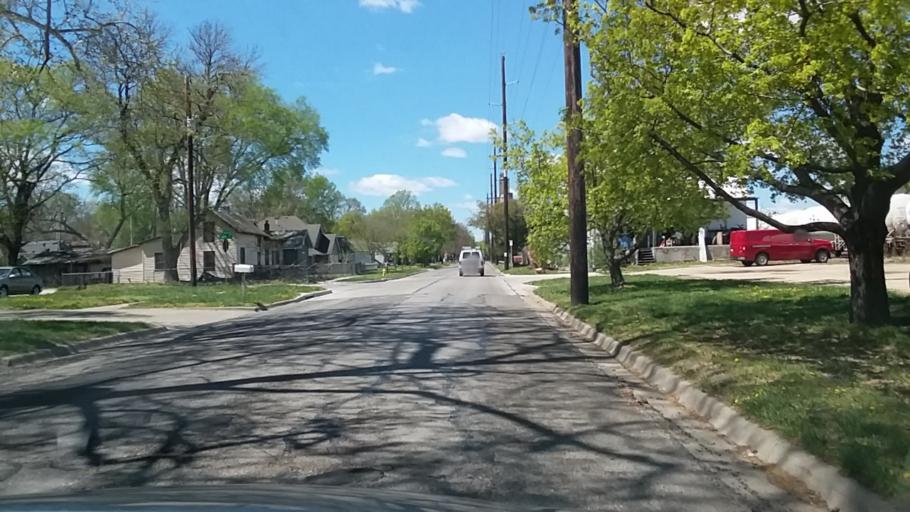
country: US
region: Kansas
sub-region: Douglas County
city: Lawrence
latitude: 38.9778
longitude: -95.2260
